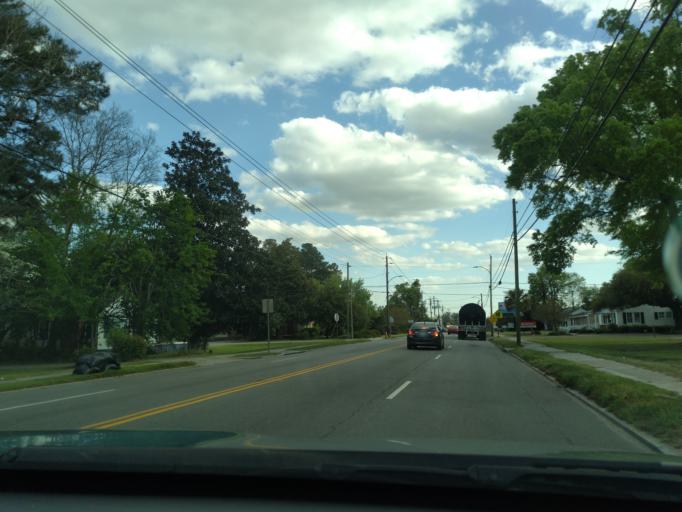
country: US
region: South Carolina
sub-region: Williamsburg County
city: Kingstree
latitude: 33.6695
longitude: -79.8356
